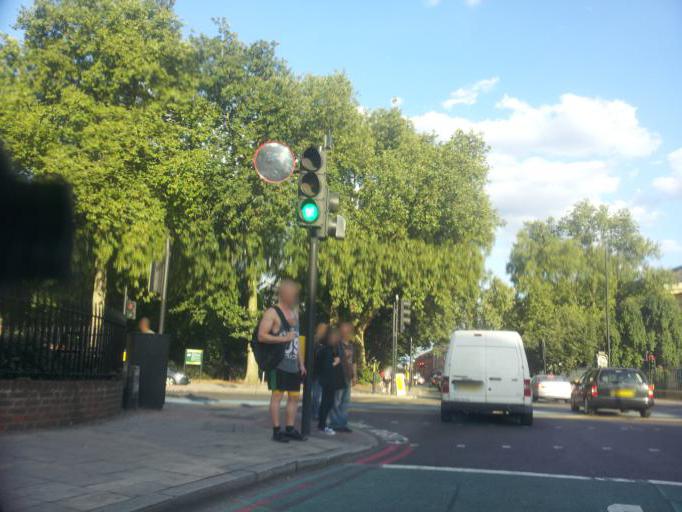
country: GB
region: England
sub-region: Greater London
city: Kennington
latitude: 51.4822
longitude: -0.1126
